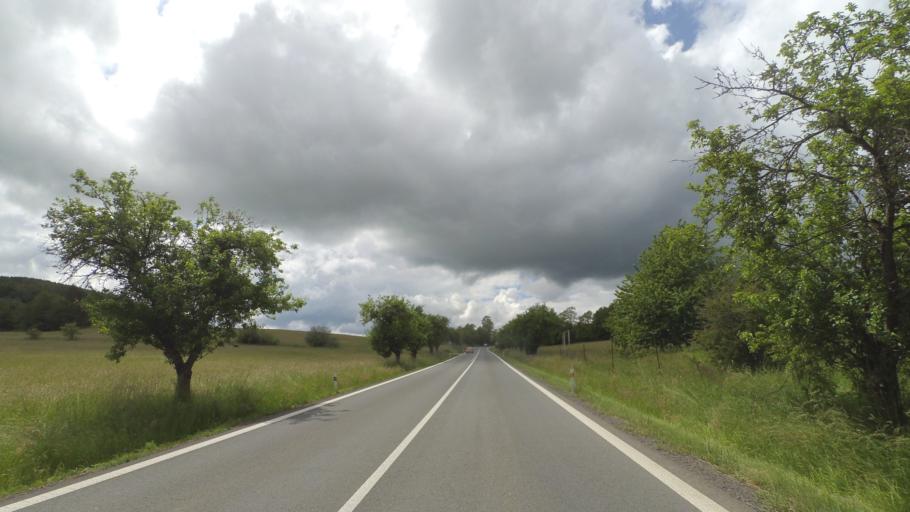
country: CZ
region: Plzensky
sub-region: Okres Domazlice
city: Kdyne
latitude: 49.3718
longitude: 13.0815
